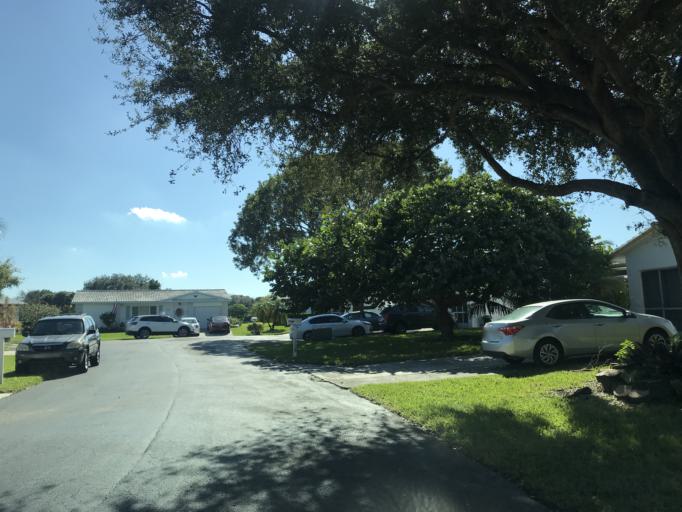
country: US
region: Florida
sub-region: Broward County
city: Plantation
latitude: 26.1364
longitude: -80.2678
